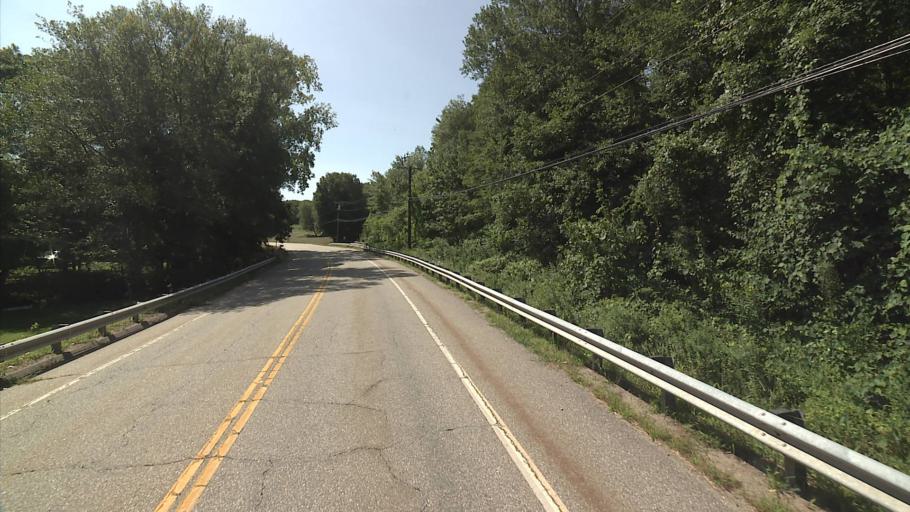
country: US
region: Connecticut
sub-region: New London County
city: Baltic
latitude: 41.6209
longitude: -72.1184
